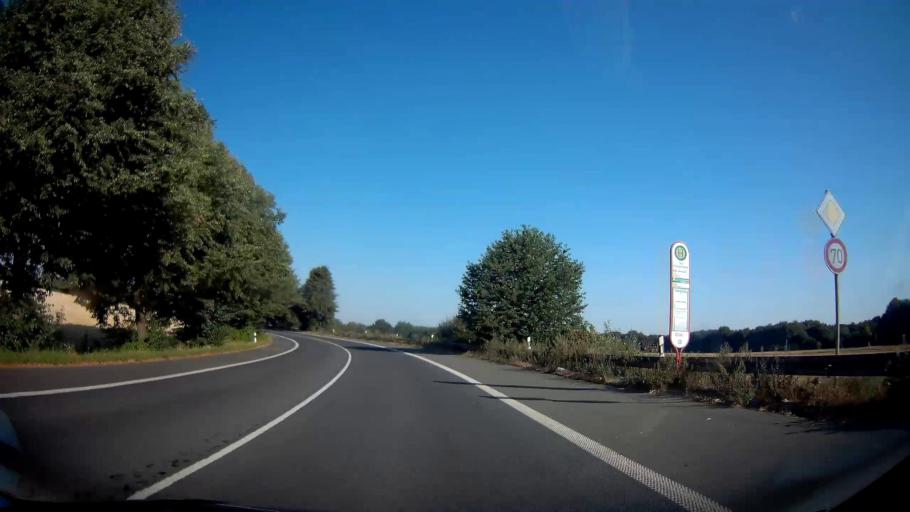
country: DE
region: North Rhine-Westphalia
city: Waltrop
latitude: 51.5630
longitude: 7.4101
